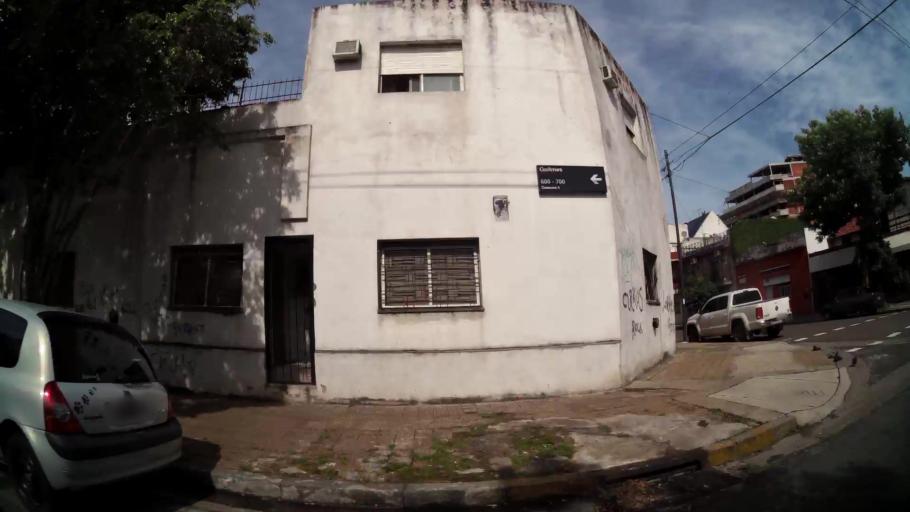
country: AR
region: Buenos Aires
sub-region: Partido de Avellaneda
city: Avellaneda
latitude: -34.6472
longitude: -58.4175
